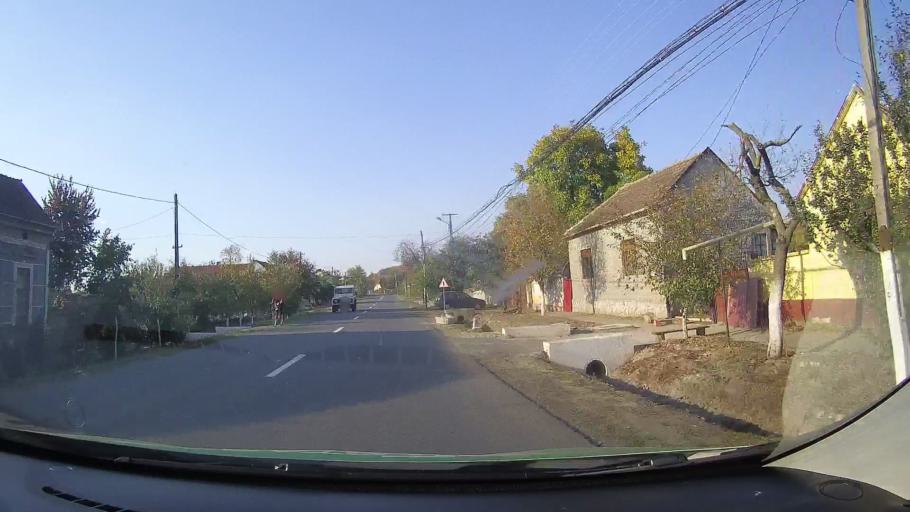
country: RO
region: Arad
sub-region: Comuna Ghioroc
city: Ghioroc
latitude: 46.1427
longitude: 21.6013
